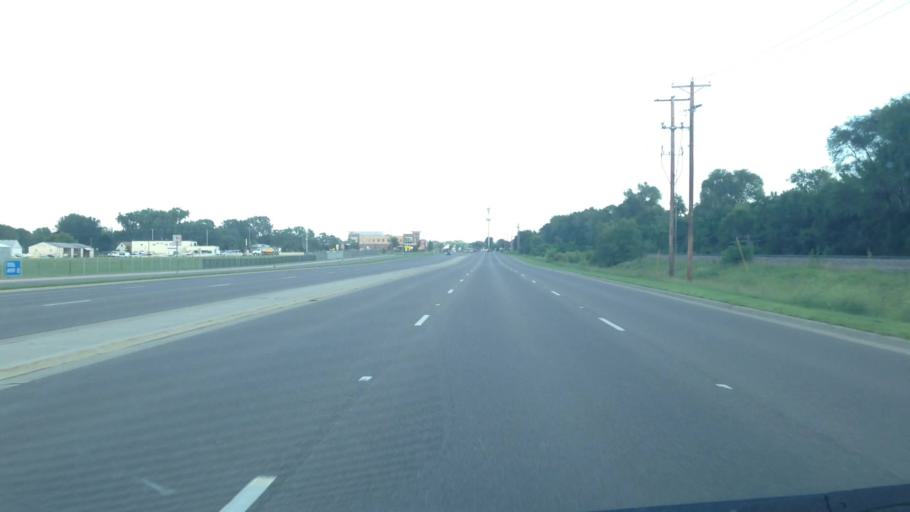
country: US
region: Minnesota
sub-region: Hennepin County
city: Crystal
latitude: 45.0611
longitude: -93.3628
